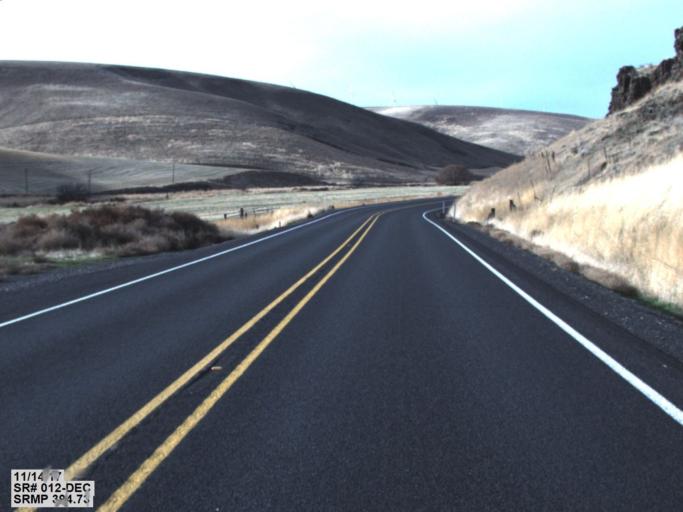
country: US
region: Washington
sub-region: Garfield County
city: Pomeroy
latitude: 46.4903
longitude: -117.7639
